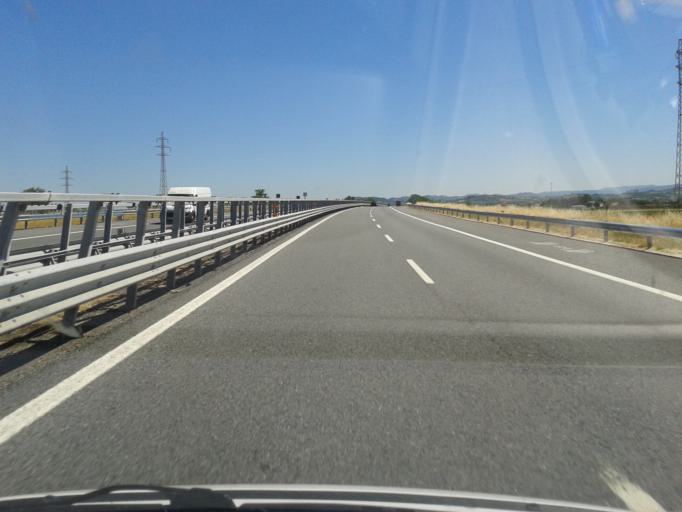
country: IT
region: Piedmont
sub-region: Provincia di Alessandria
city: Pozzolo Formigaro
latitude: 44.8244
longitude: 8.7918
